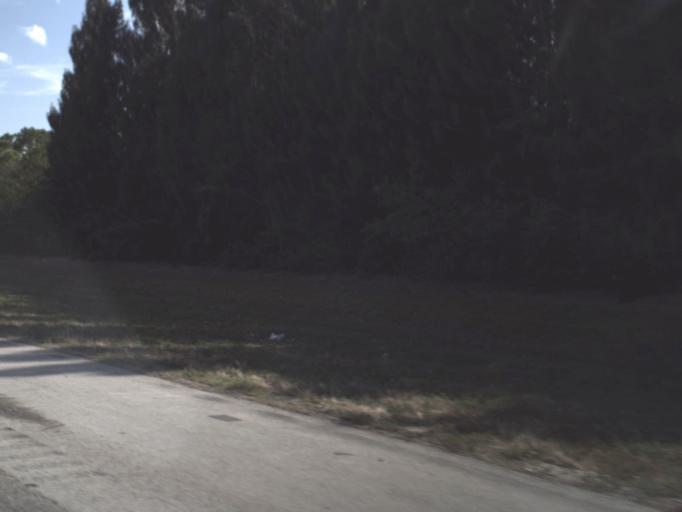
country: US
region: Florida
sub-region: Brevard County
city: June Park
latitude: 28.1376
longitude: -80.7061
